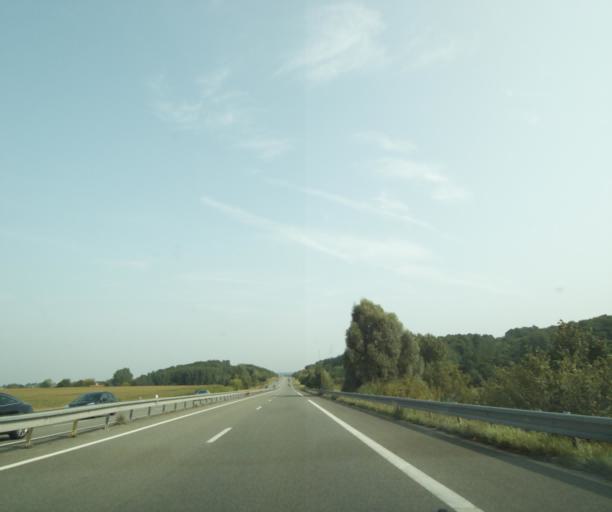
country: FR
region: Pays de la Loire
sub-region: Departement de la Sarthe
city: Sainte-Jamme-sur-Sarthe
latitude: 48.1396
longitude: 0.1437
